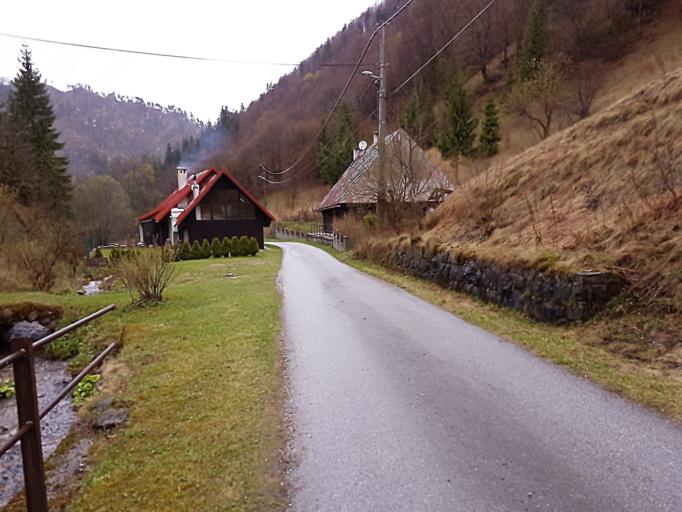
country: SK
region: Banskobystricky
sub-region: Okres Banska Bystrica
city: Banska Bystrica
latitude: 48.8495
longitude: 19.1559
